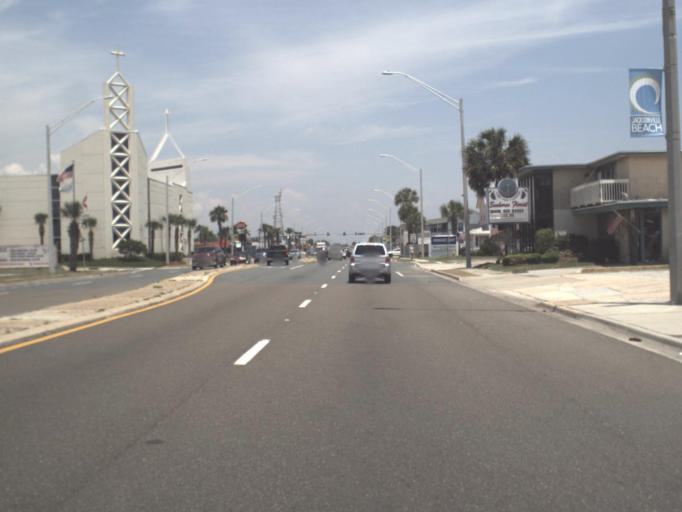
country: US
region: Florida
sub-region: Duval County
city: Jacksonville Beach
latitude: 30.2947
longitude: -81.3930
